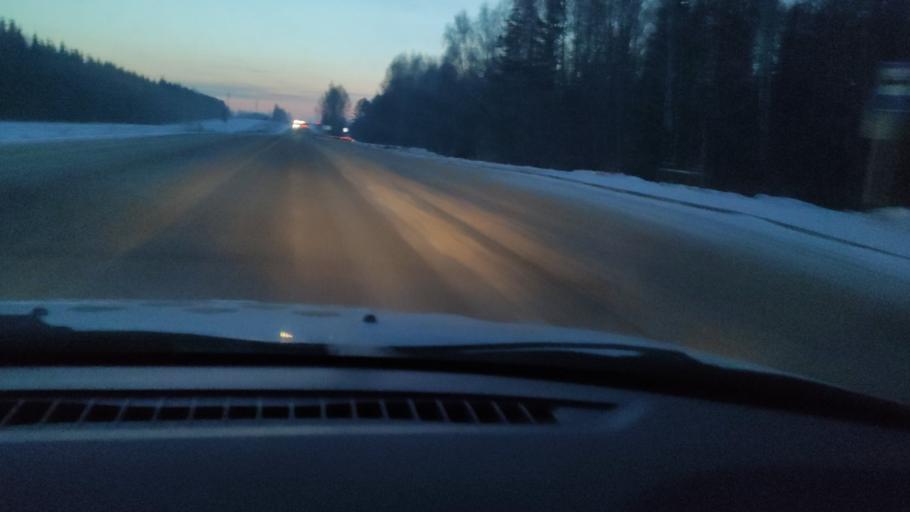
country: RU
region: Perm
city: Kungur
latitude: 57.4095
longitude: 56.9049
